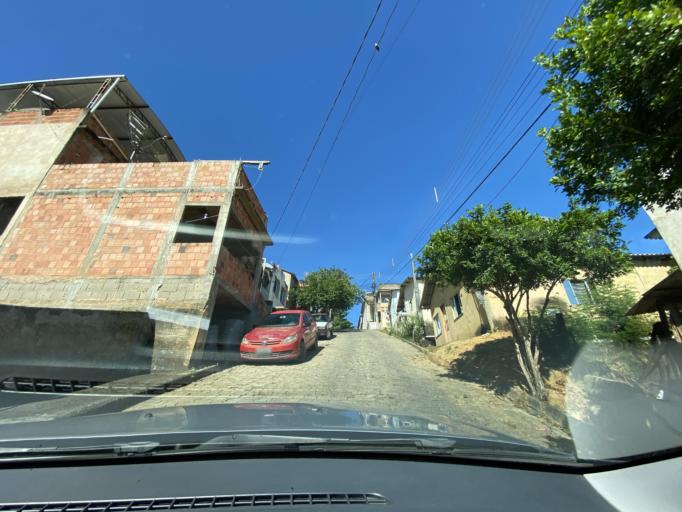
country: BR
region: Espirito Santo
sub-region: Jeronimo Monteiro
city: Jeronimo Monteiro
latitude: -20.7931
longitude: -41.3989
